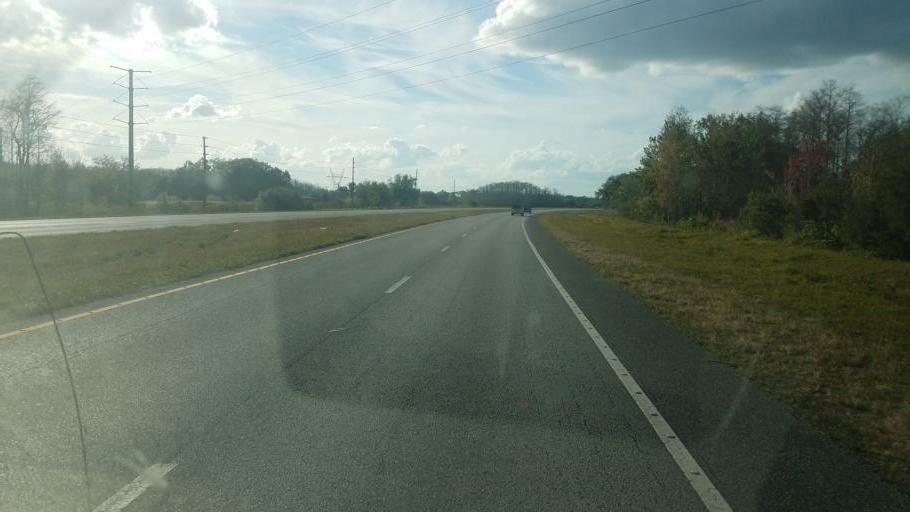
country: US
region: Florida
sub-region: Osceola County
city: Saint Cloud
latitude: 28.1450
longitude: -81.0865
